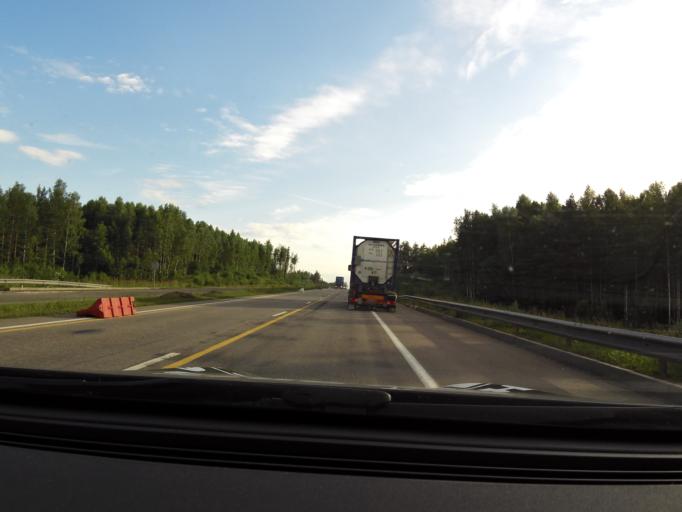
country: RU
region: Vladimir
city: Sudogda
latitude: 56.1219
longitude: 40.8588
